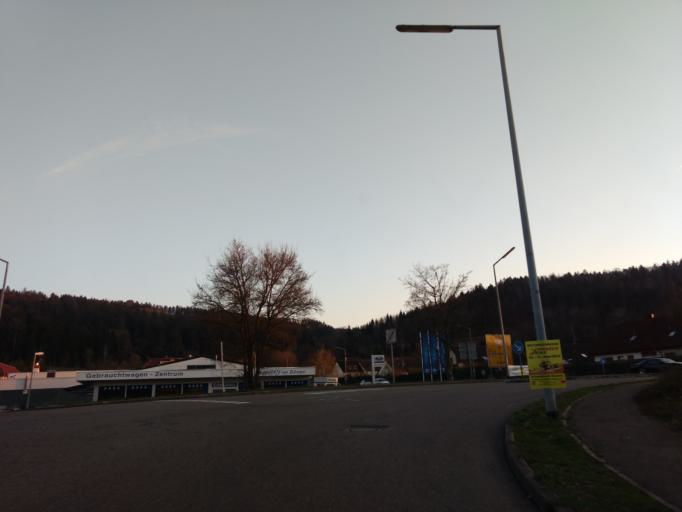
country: DE
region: Baden-Wuerttemberg
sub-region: Regierungsbezirk Stuttgart
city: Lorch
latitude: 48.7958
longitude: 9.7033
